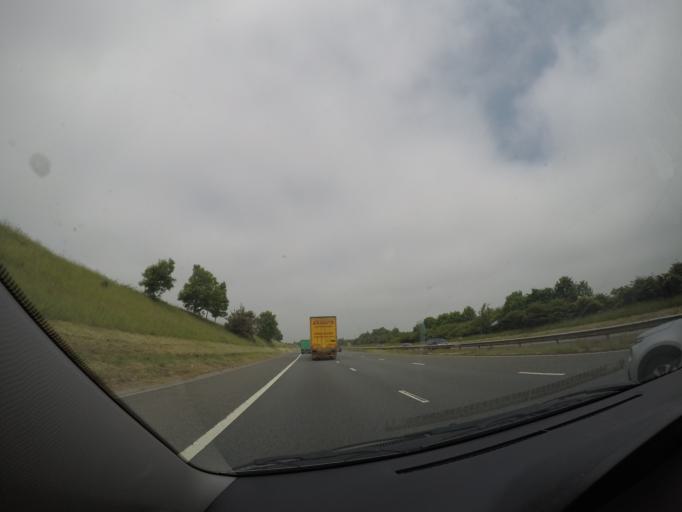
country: GB
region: England
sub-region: North Yorkshire
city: Boroughbridge
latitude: 54.0431
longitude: -1.3863
